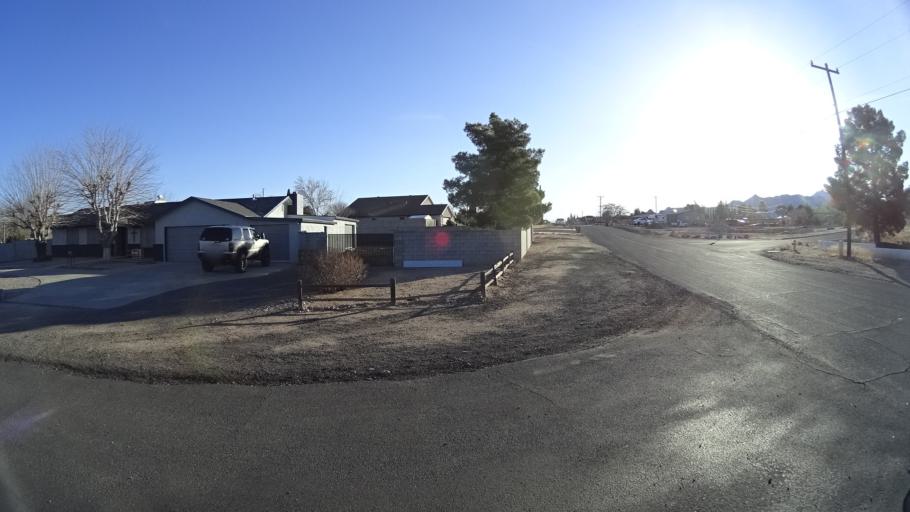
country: US
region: Arizona
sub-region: Mohave County
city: Kingman
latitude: 35.2032
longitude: -114.0074
